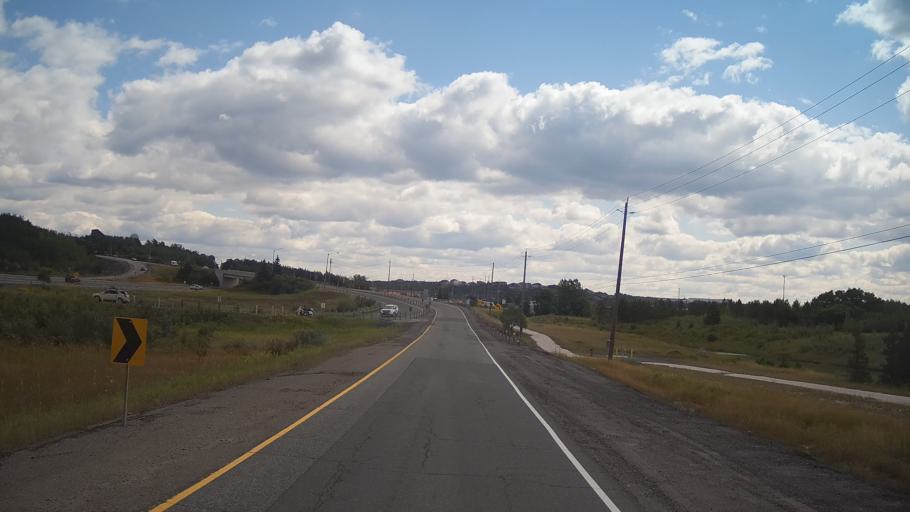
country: CA
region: Ontario
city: Greater Sudbury
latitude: 46.4719
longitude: -81.0436
